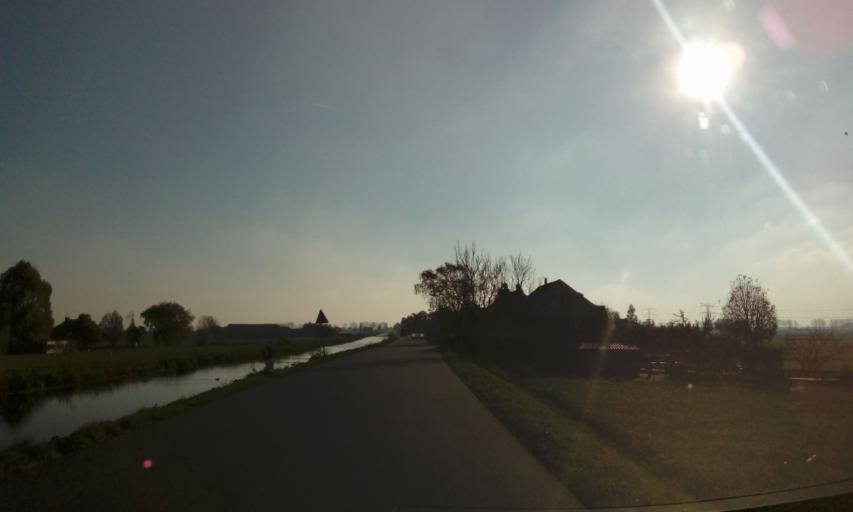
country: NL
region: South Holland
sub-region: Gemeente Rijnwoude
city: Benthuizen
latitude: 52.0409
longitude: 4.5765
